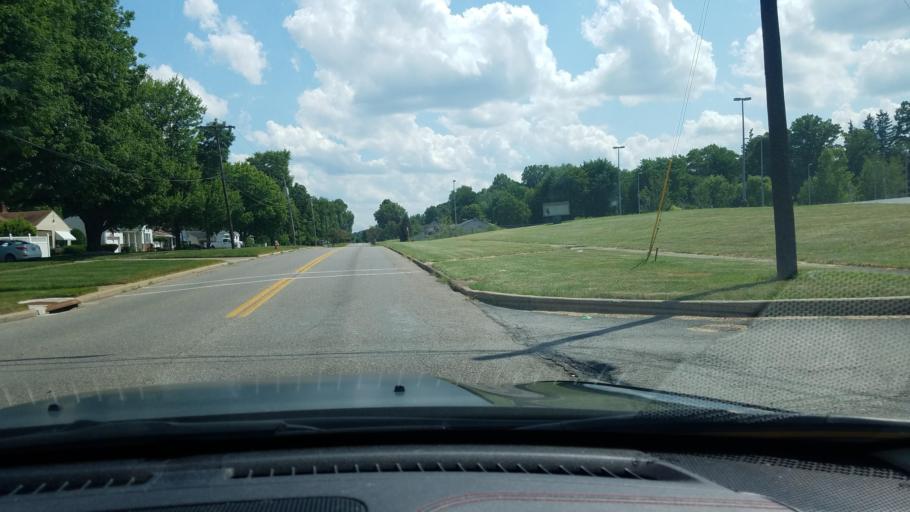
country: US
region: Ohio
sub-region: Mahoning County
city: Youngstown
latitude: 41.0774
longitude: -80.6998
